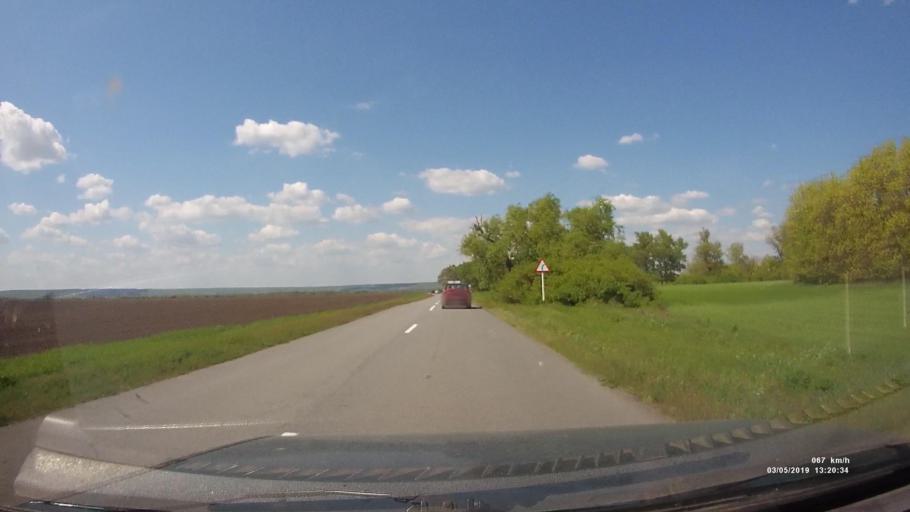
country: RU
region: Rostov
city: Semikarakorsk
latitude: 47.5475
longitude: 40.7526
